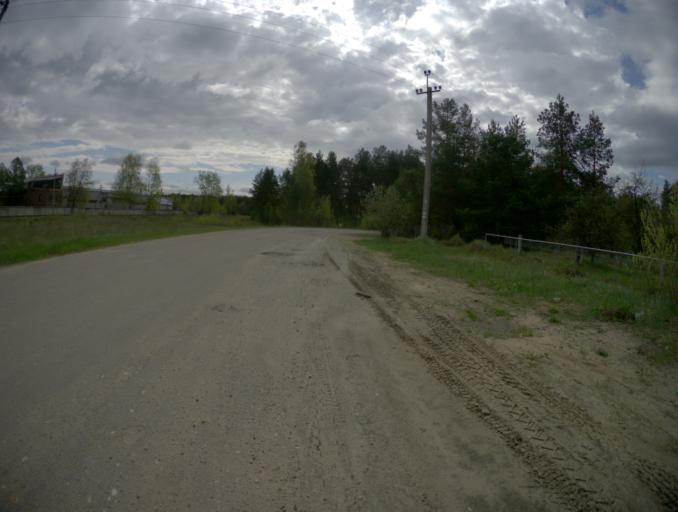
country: RU
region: Vladimir
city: Golovino
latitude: 55.9466
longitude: 40.4443
